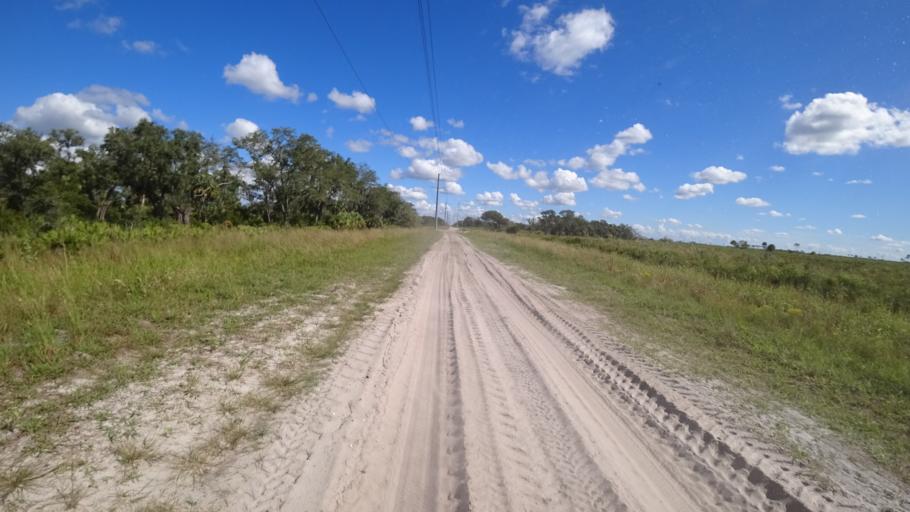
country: US
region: Florida
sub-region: Sarasota County
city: Lake Sarasota
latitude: 27.2443
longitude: -82.2702
